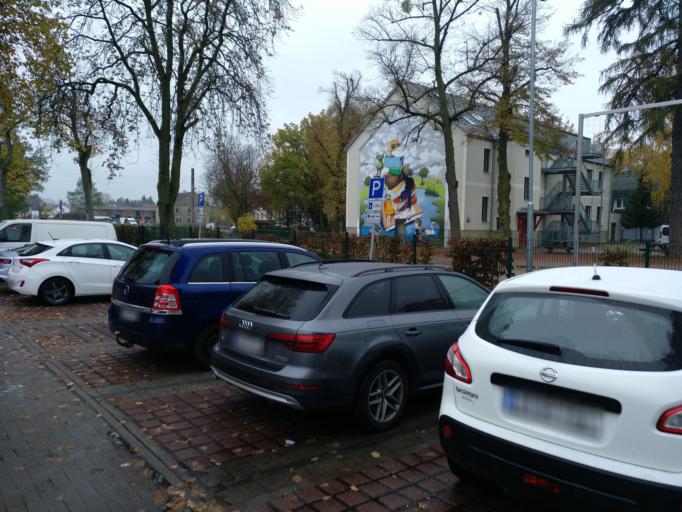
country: DE
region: Brandenburg
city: Neuenhagen
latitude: 52.5155
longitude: 13.7119
